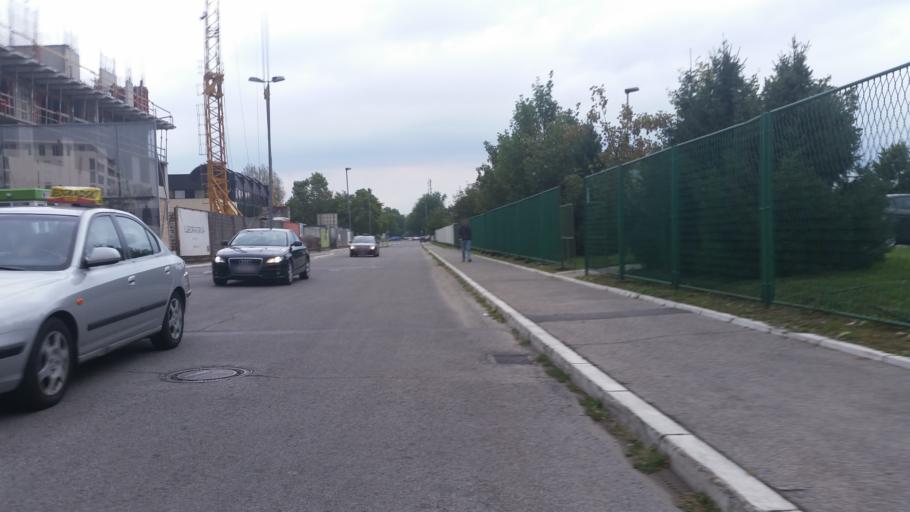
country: RS
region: Central Serbia
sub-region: Belgrade
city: Novi Beograd
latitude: 44.8124
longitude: 20.3995
